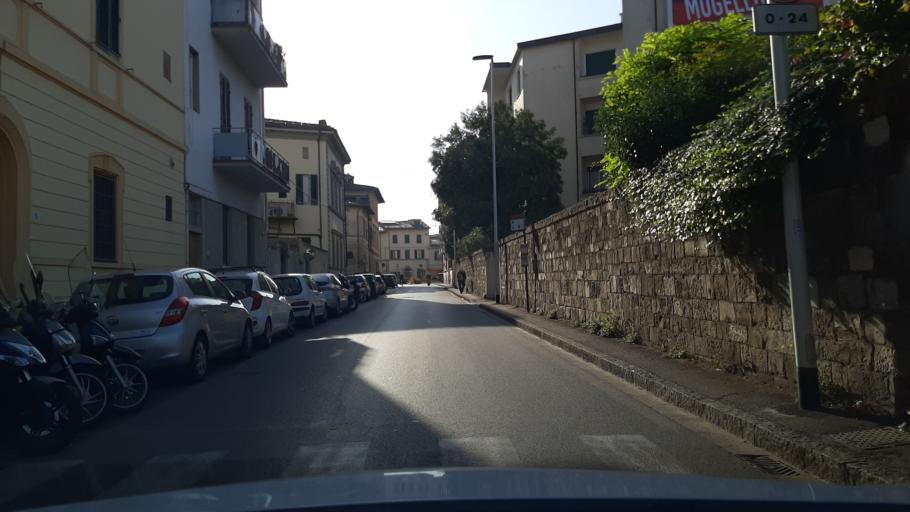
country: IT
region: Tuscany
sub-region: Province of Florence
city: Fiesole
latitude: 43.7730
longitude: 11.2828
